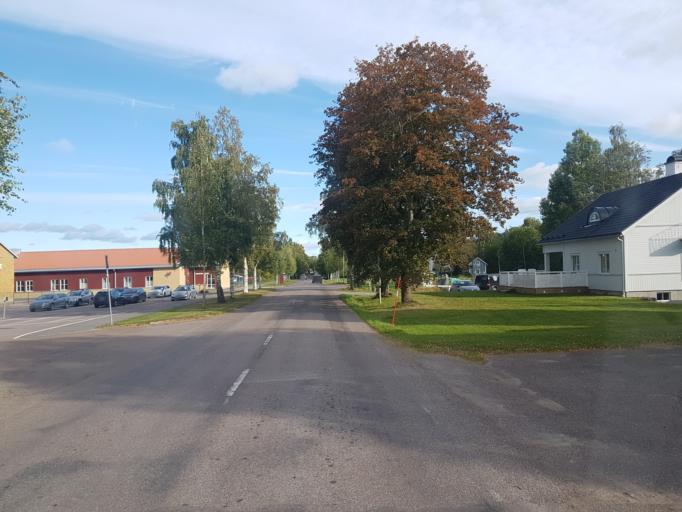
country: SE
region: Dalarna
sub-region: Borlange Kommun
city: Ornas
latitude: 60.4144
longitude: 15.6031
